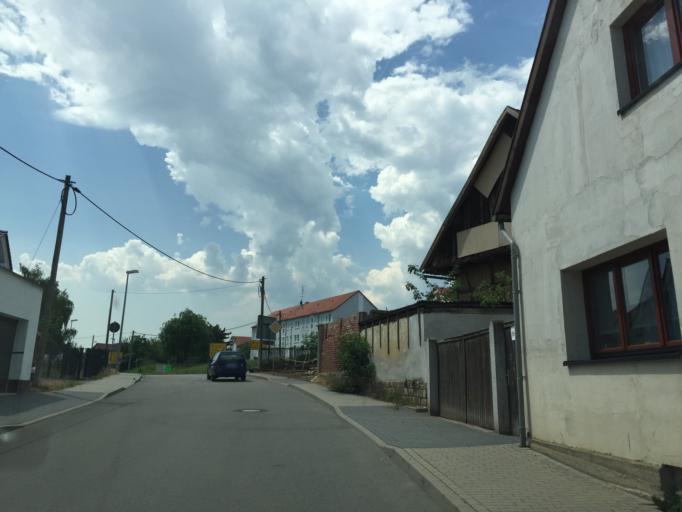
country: DE
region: Thuringia
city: Alkersleben
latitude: 50.8235
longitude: 11.0151
